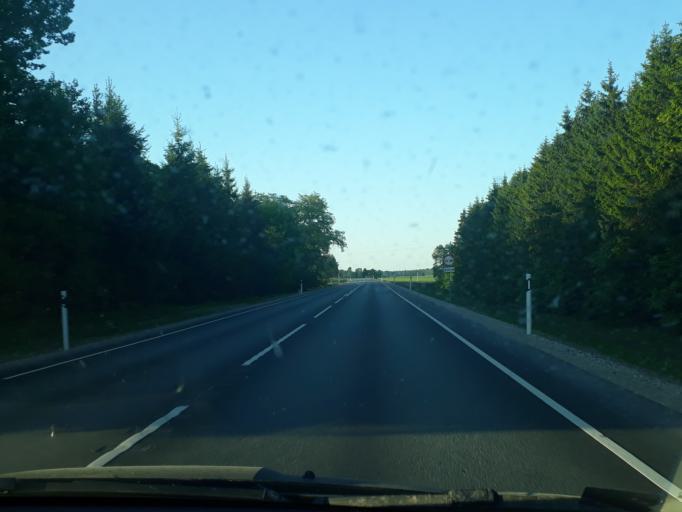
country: EE
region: Paernumaa
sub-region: Tootsi vald
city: Tootsi
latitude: 58.5422
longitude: 24.8425
